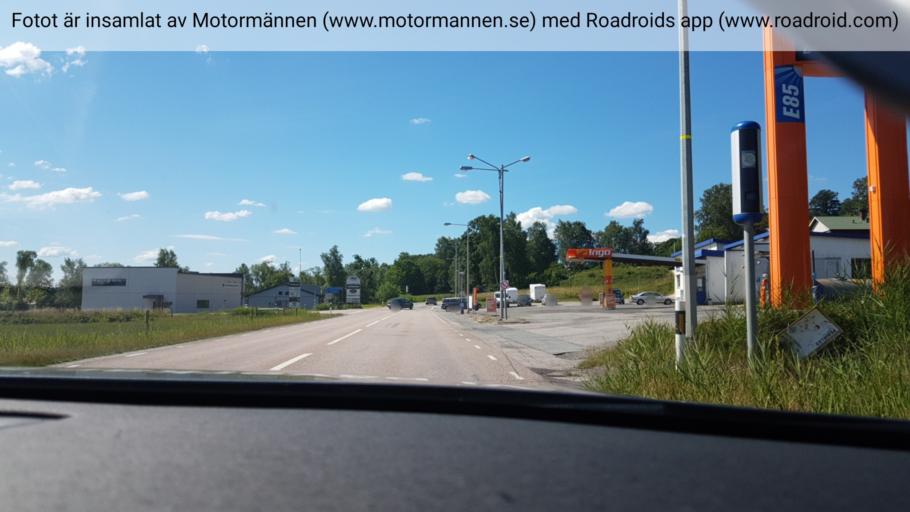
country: SE
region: Vaestra Goetaland
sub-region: Marks Kommun
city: Horred
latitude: 57.3608
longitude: 12.4826
